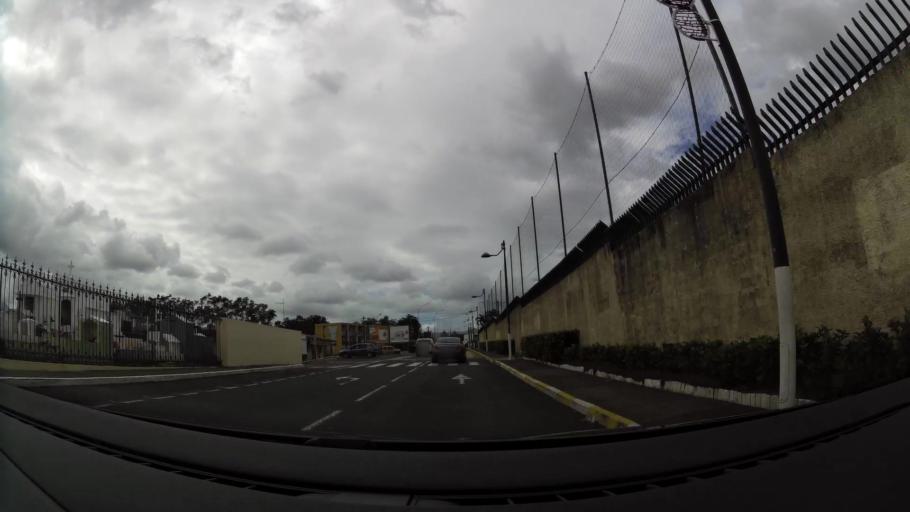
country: GP
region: Guadeloupe
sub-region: Guadeloupe
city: Lamentin
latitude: 16.2714
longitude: -61.6340
